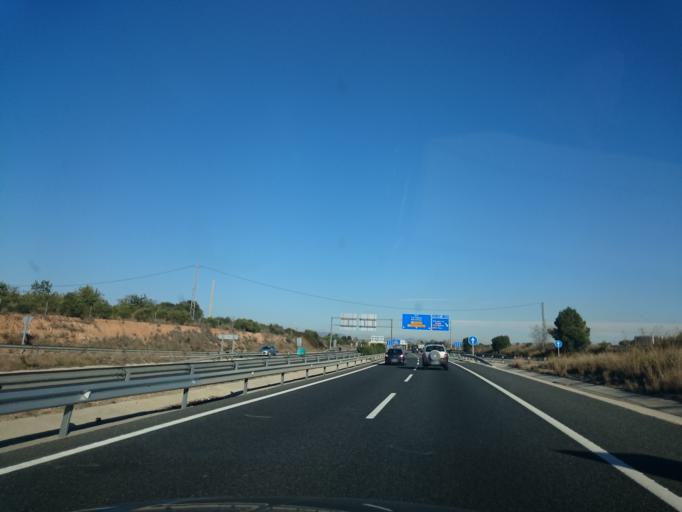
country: ES
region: Catalonia
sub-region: Provincia de Tarragona
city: Vila-seca
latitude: 41.1066
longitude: 1.1560
